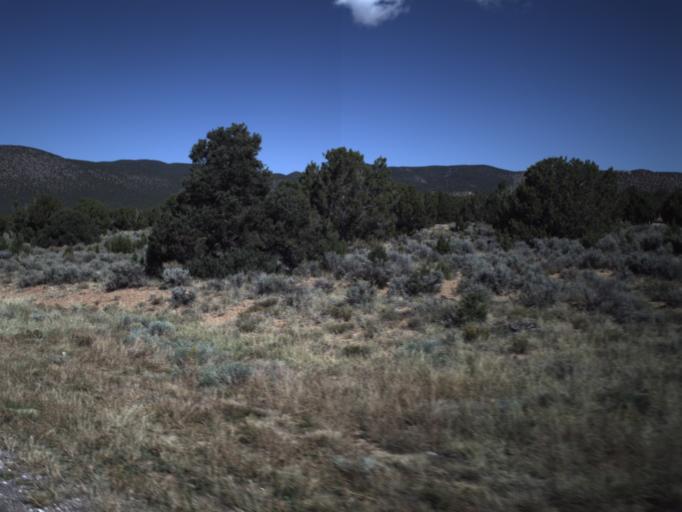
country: US
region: Utah
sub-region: Washington County
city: Enterprise
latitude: 37.6335
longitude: -113.4297
